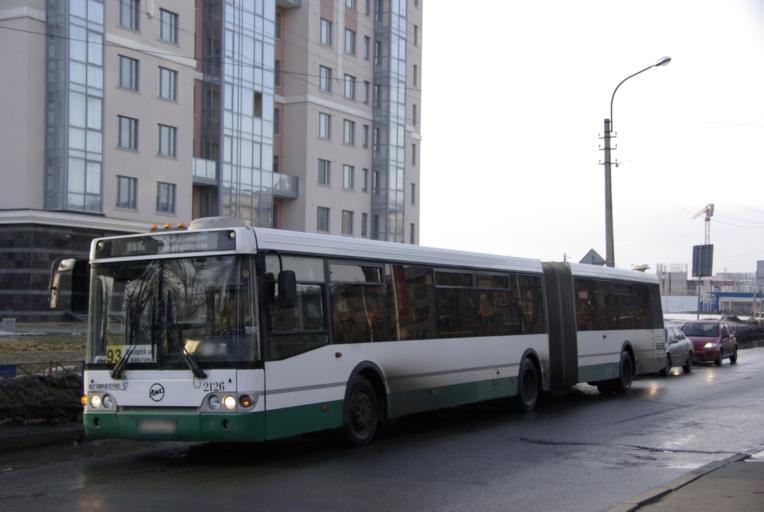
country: RU
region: Leningrad
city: Krestovskiy ostrov
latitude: 59.9841
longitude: 30.2567
